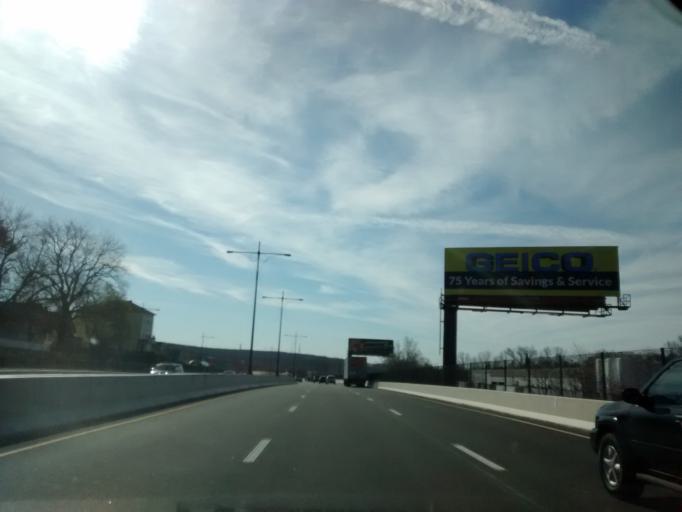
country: US
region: Massachusetts
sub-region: Worcester County
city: Worcester
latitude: 42.2396
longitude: -71.8007
